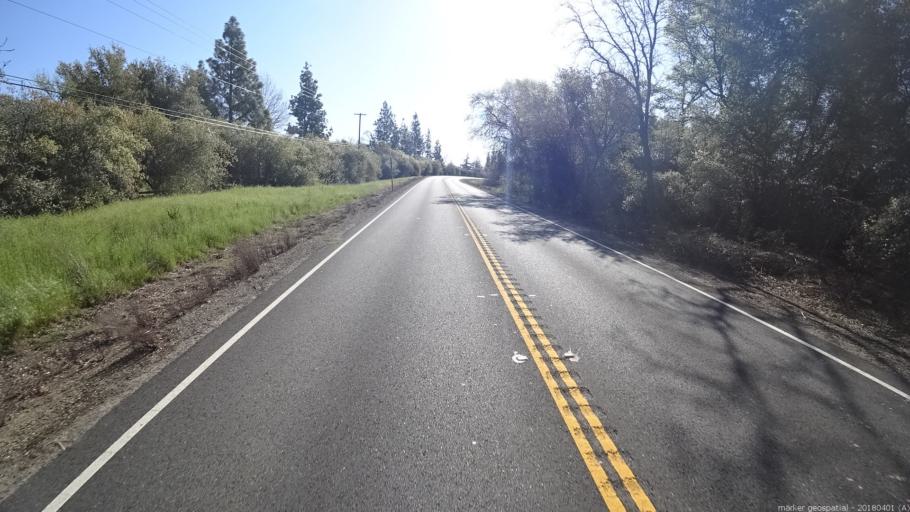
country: US
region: California
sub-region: Sacramento County
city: Rancho Murieta
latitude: 38.4905
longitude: -121.0887
